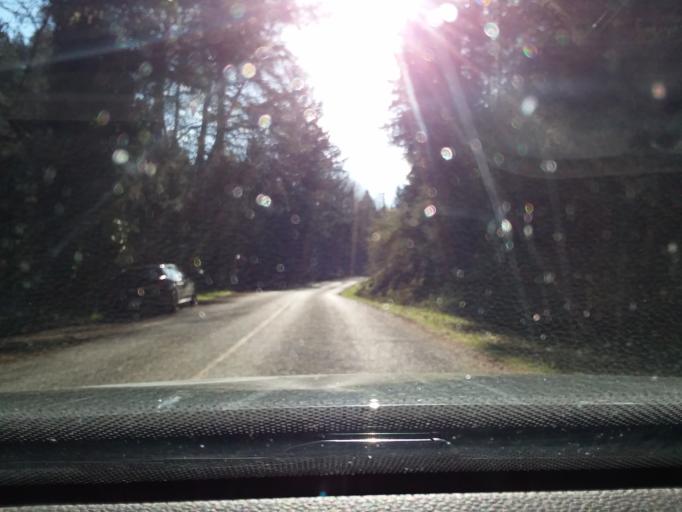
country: CA
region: British Columbia
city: North Cowichan
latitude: 48.9417
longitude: -123.4987
